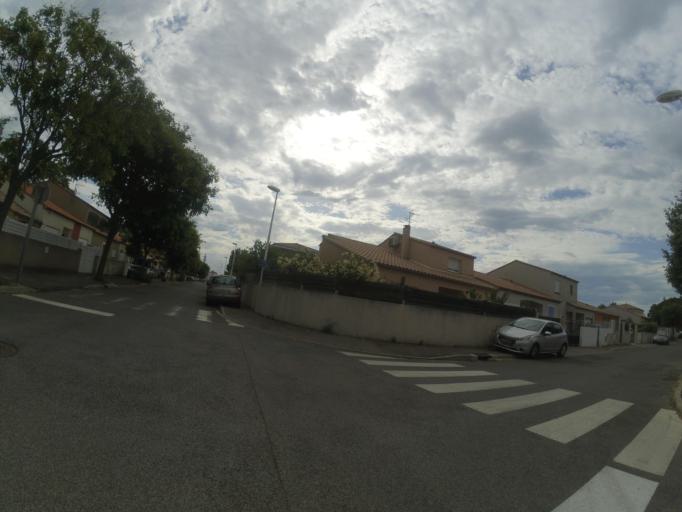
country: FR
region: Languedoc-Roussillon
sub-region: Departement des Pyrenees-Orientales
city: Toulouges
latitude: 42.6754
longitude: 2.8430
